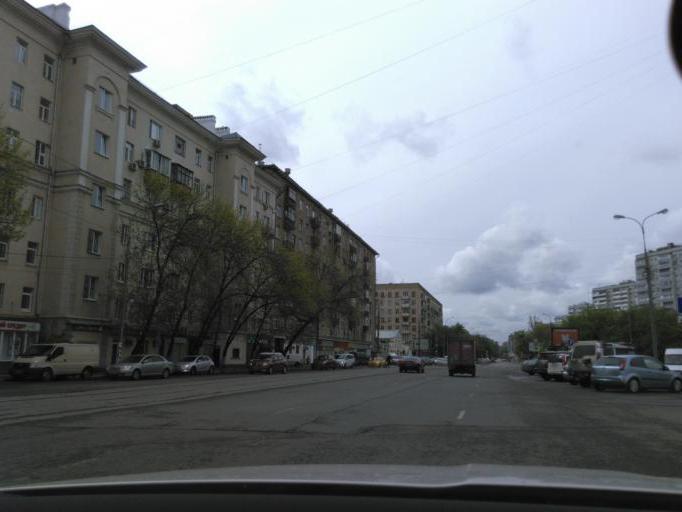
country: RU
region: Moscow
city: Taganskiy
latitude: 55.7460
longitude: 37.6794
